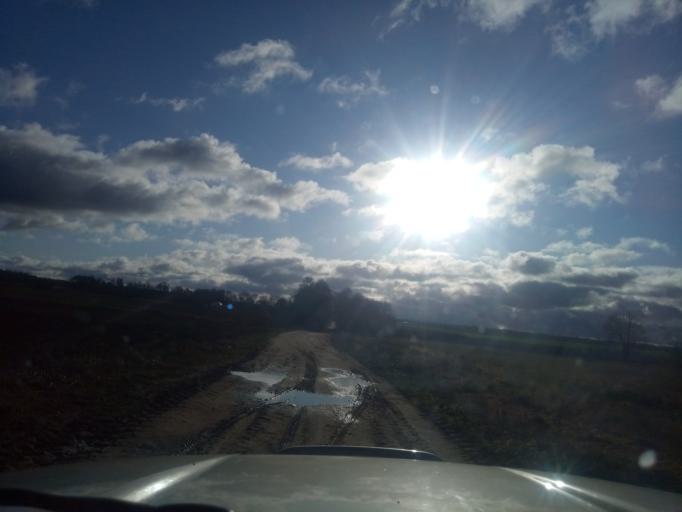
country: BY
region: Minsk
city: Tsimkavichy
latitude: 53.1842
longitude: 26.9061
